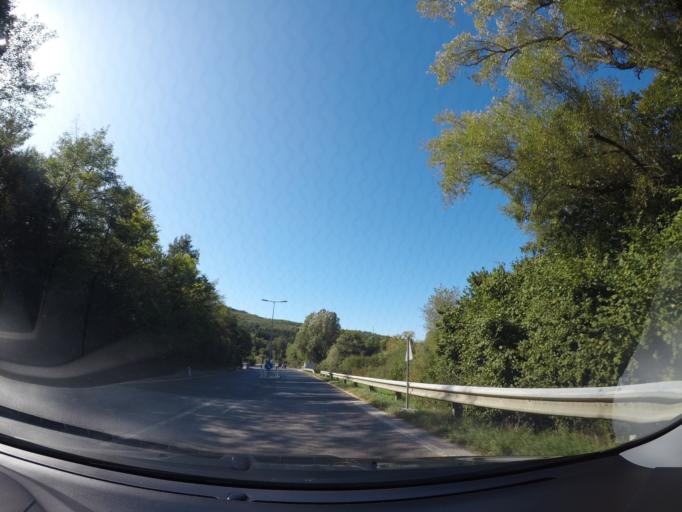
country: AT
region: Lower Austria
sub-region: Politischer Bezirk Wien-Umgebung
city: Wolfsgraben
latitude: 48.1706
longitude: 16.1277
